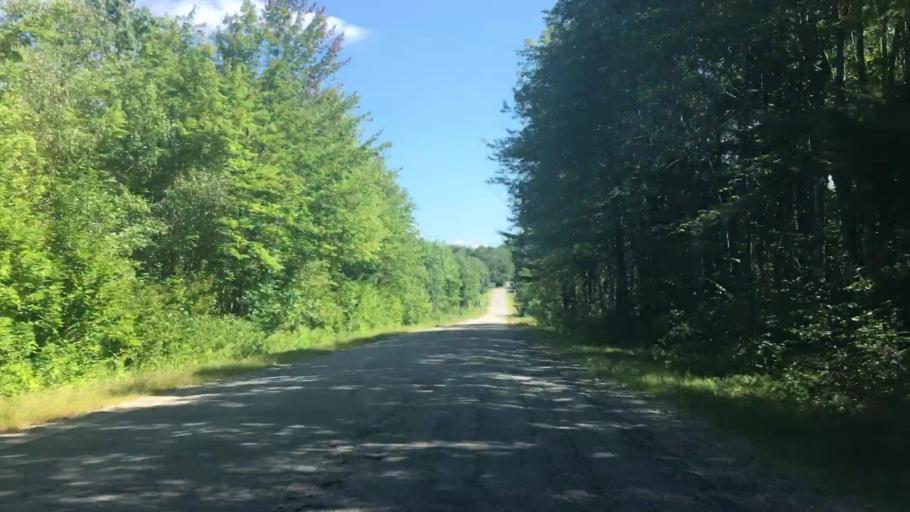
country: US
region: Maine
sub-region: Androscoggin County
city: Sabattus
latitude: 44.1234
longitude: -70.0658
